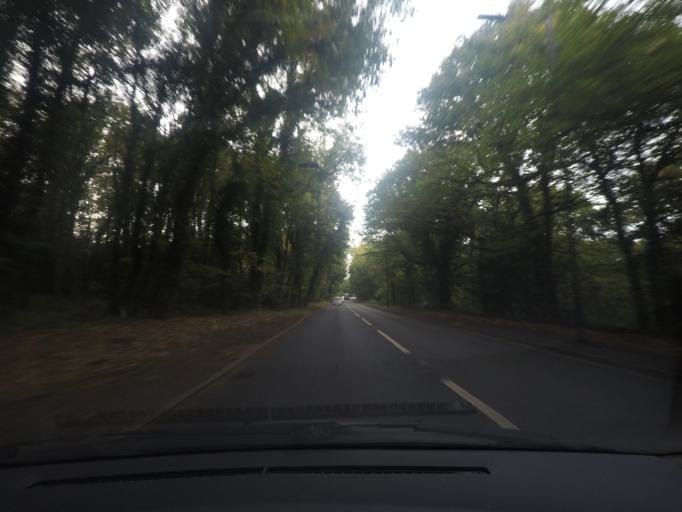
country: GB
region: England
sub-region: Sheffield
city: Chapletown
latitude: 53.4617
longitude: -1.5017
